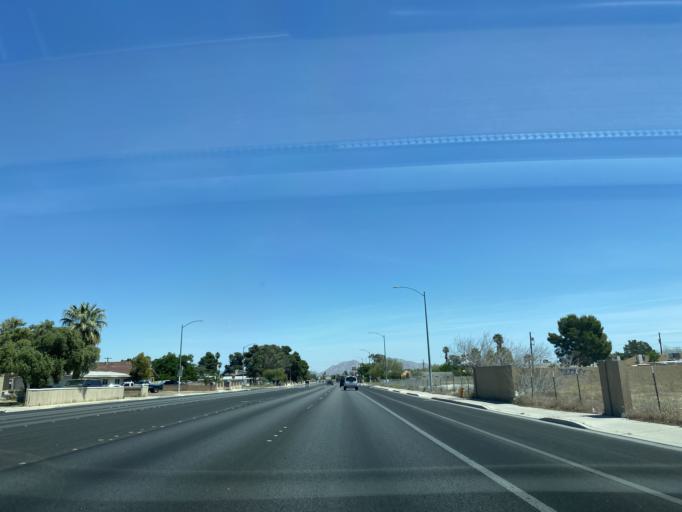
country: US
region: Nevada
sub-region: Clark County
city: Las Vegas
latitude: 36.1955
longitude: -115.2121
